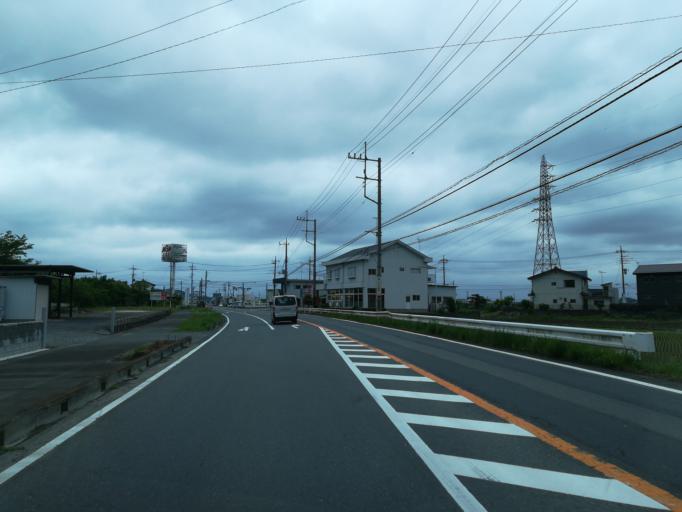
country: JP
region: Ibaraki
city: Tsukuba
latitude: 36.1808
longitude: 140.0799
